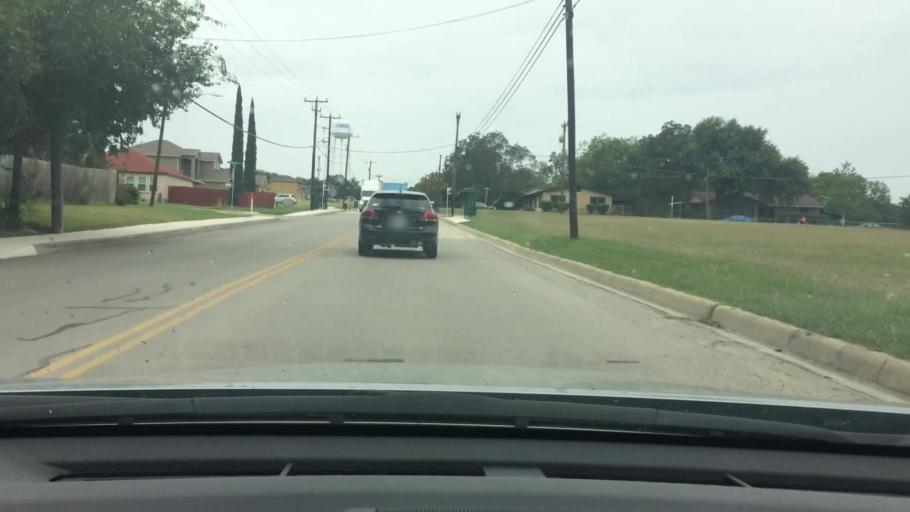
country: US
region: Texas
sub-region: Bexar County
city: Converse
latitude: 29.5230
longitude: -98.3202
